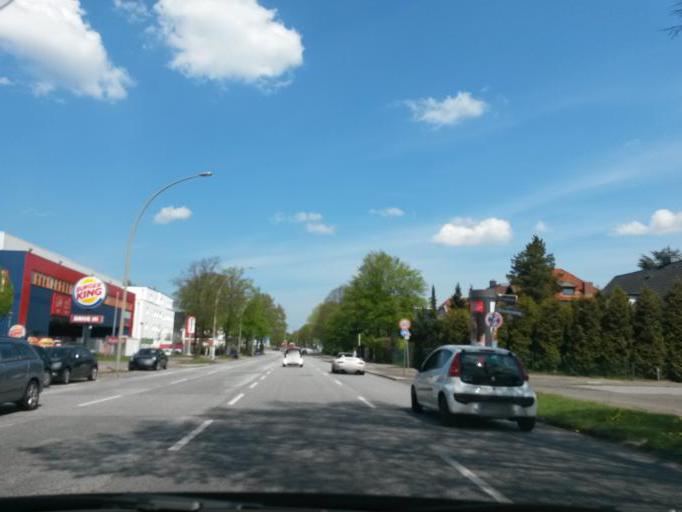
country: DE
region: Hamburg
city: Alsterdorf
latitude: 53.6157
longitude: 10.0036
